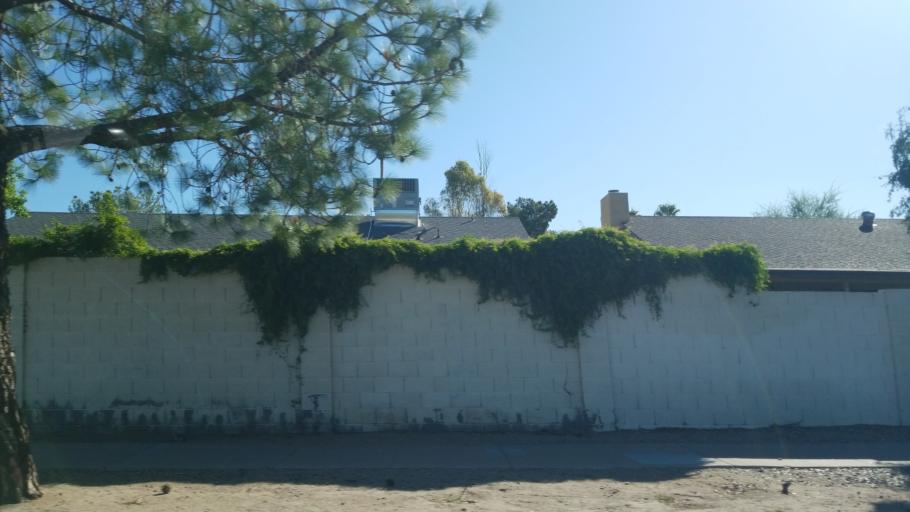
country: US
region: Arizona
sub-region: Maricopa County
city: Glendale
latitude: 33.5115
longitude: -112.2204
